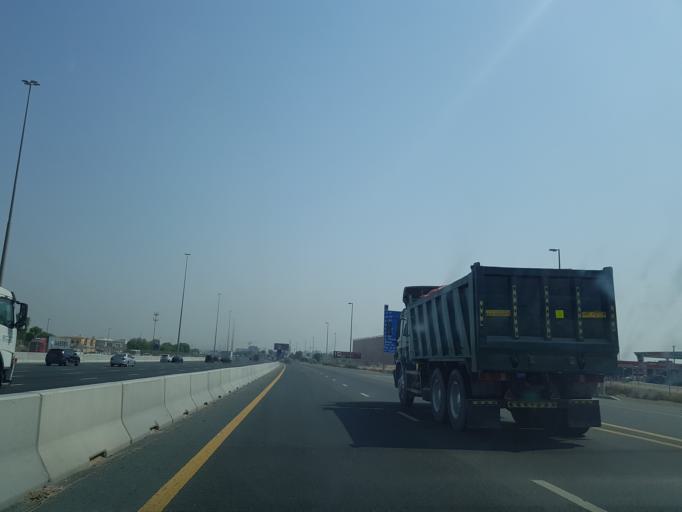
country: AE
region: Ash Shariqah
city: Sharjah
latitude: 25.1326
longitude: 55.3789
